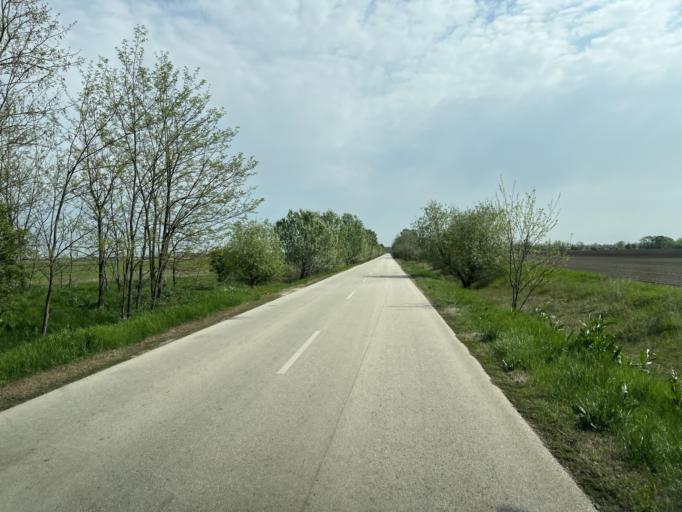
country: HU
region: Pest
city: Jaszkarajeno
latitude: 47.0749
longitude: 20.0032
